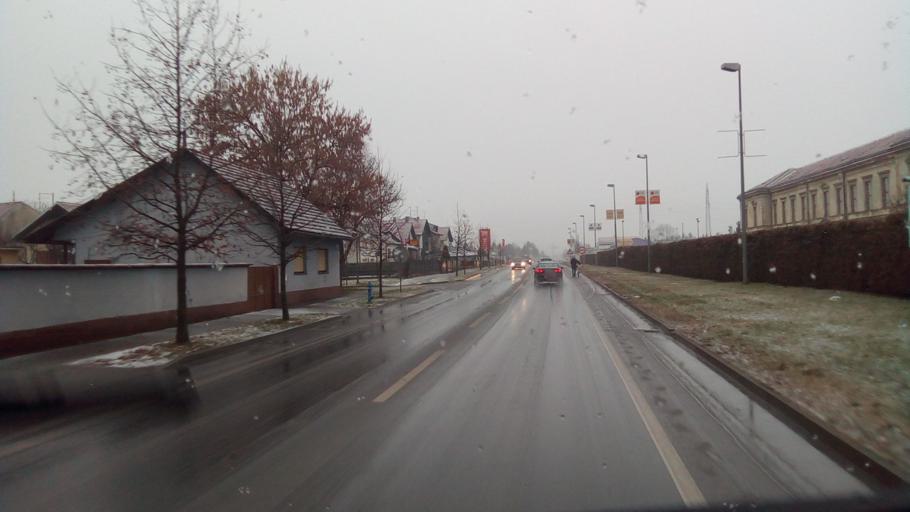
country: HR
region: Varazdinska
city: Varazdin
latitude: 46.3169
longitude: 16.3191
